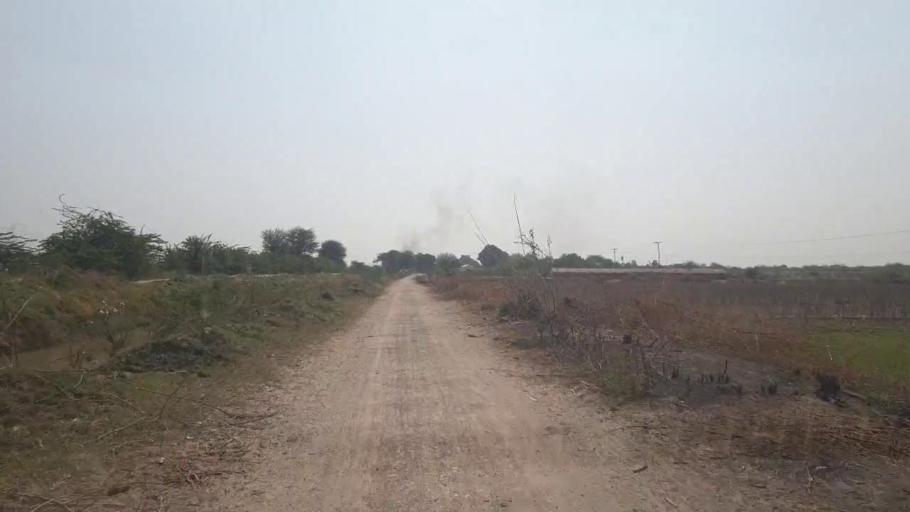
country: PK
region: Sindh
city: Dhoro Naro
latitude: 25.5062
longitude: 69.5435
